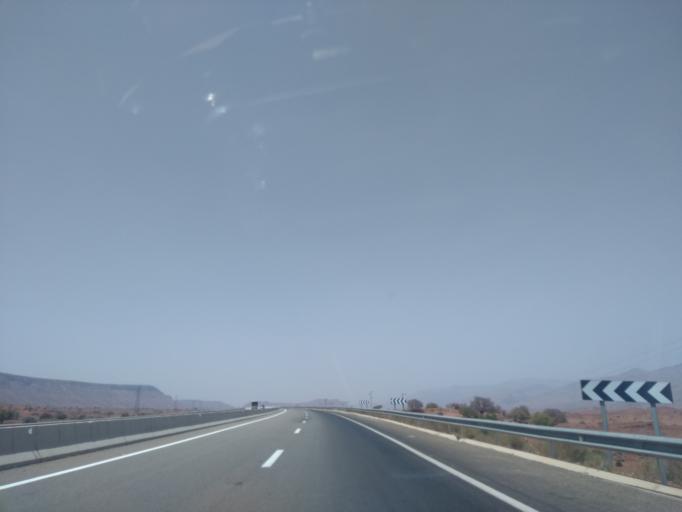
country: MA
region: Marrakech-Tensift-Al Haouz
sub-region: Chichaoua
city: Timezgadiouine
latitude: 30.8791
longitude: -9.0802
